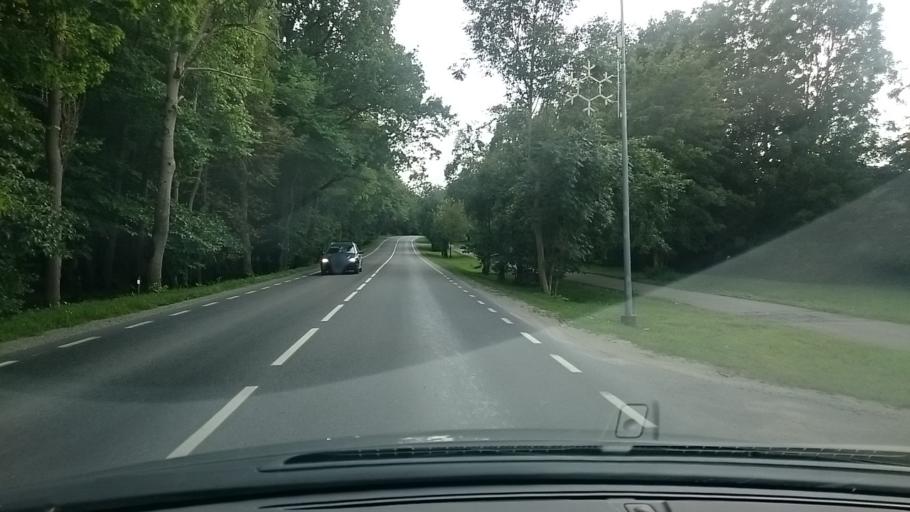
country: EE
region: Harju
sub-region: Saue vald
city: Laagri
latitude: 59.3871
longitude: 24.5777
